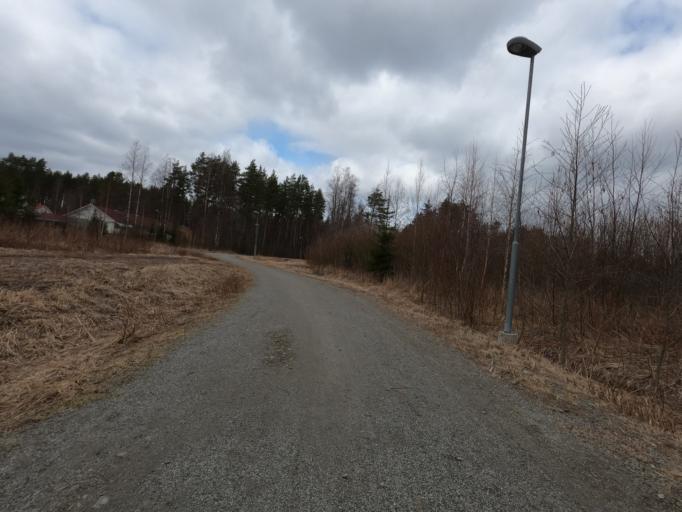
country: FI
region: North Karelia
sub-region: Joensuu
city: Joensuu
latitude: 62.5718
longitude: 29.8130
